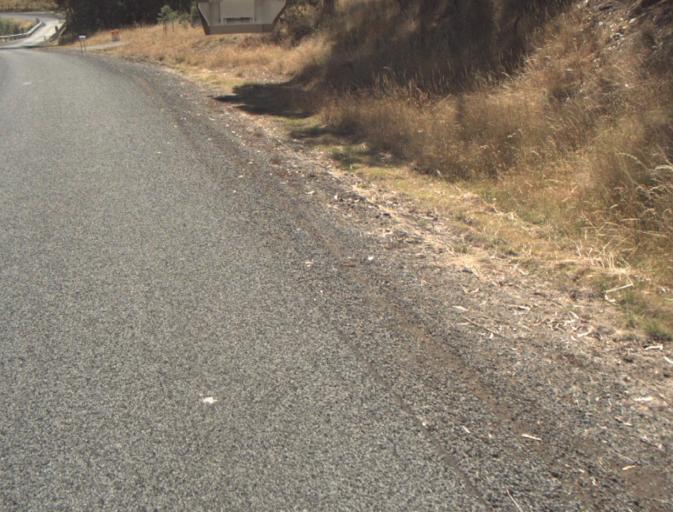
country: AU
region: Tasmania
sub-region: Launceston
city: Newstead
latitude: -41.3669
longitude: 147.3035
